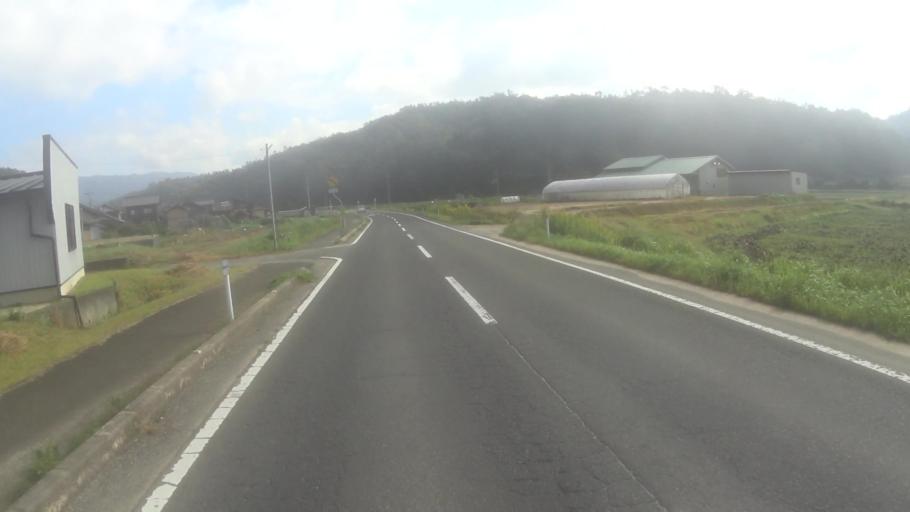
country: JP
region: Kyoto
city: Miyazu
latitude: 35.5814
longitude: 135.1271
